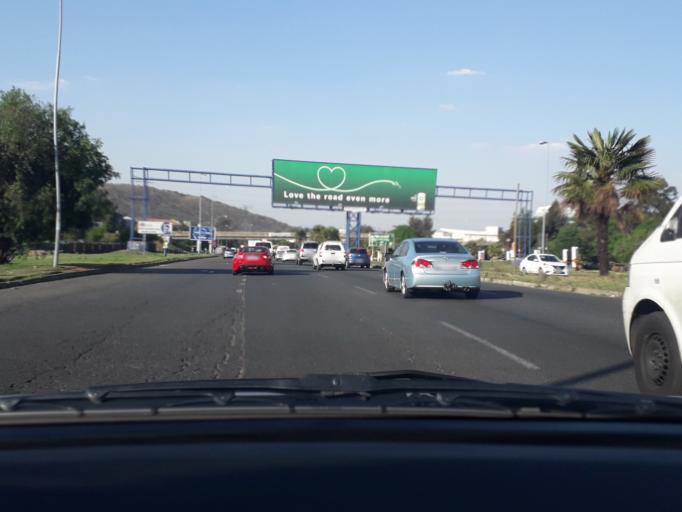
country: ZA
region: Gauteng
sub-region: City of Johannesburg Metropolitan Municipality
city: Johannesburg
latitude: -26.1813
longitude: 28.1124
